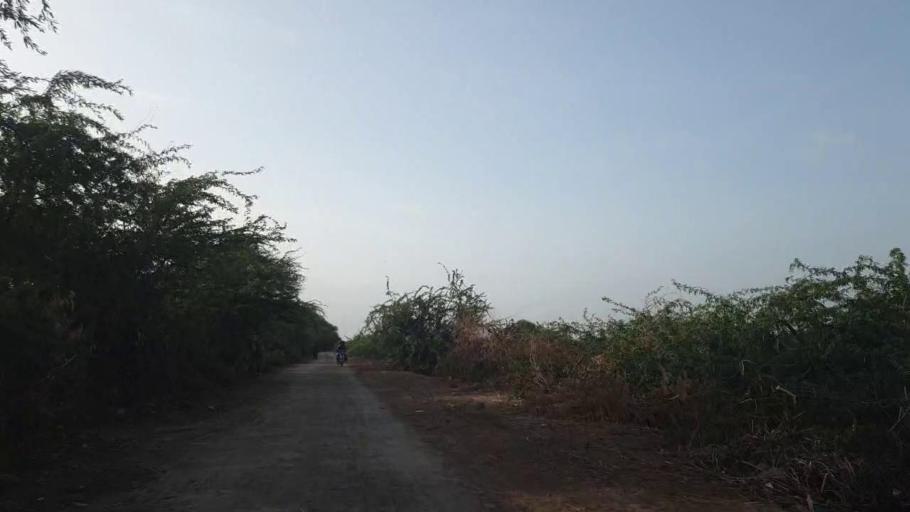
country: PK
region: Sindh
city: Kadhan
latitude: 24.6333
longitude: 69.1582
